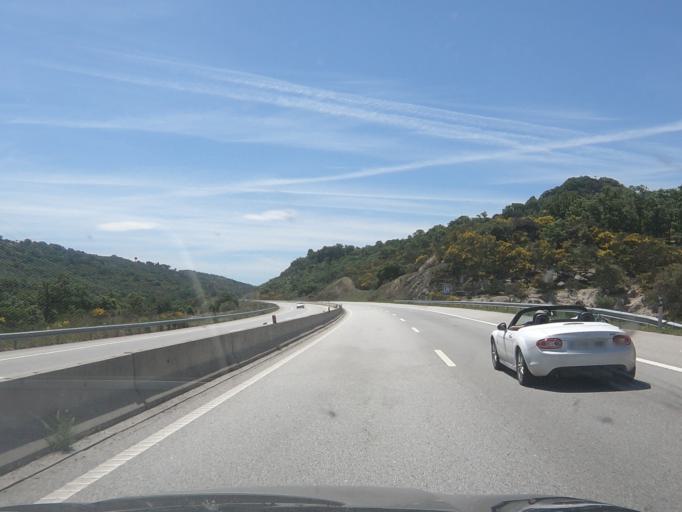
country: PT
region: Guarda
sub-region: Guarda
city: Sequeira
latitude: 40.5926
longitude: -7.2594
